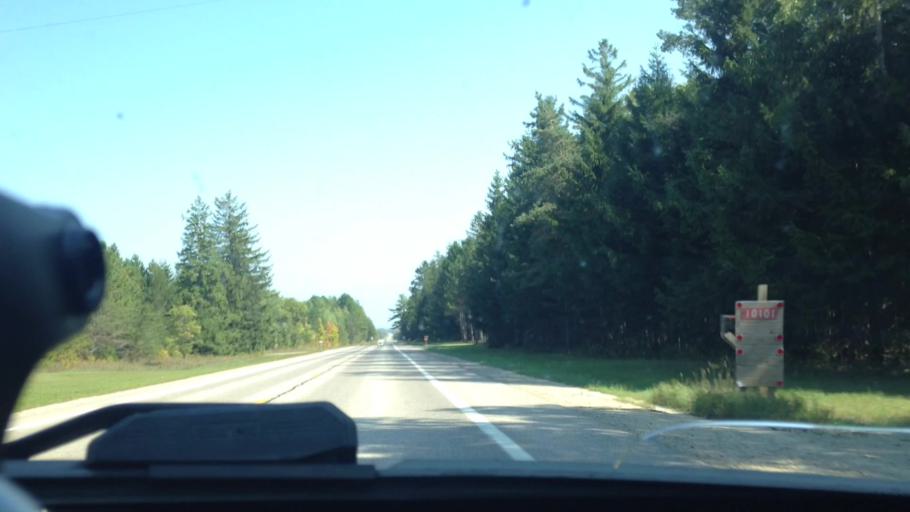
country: US
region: Michigan
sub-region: Luce County
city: Newberry
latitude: 46.3036
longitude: -85.4283
